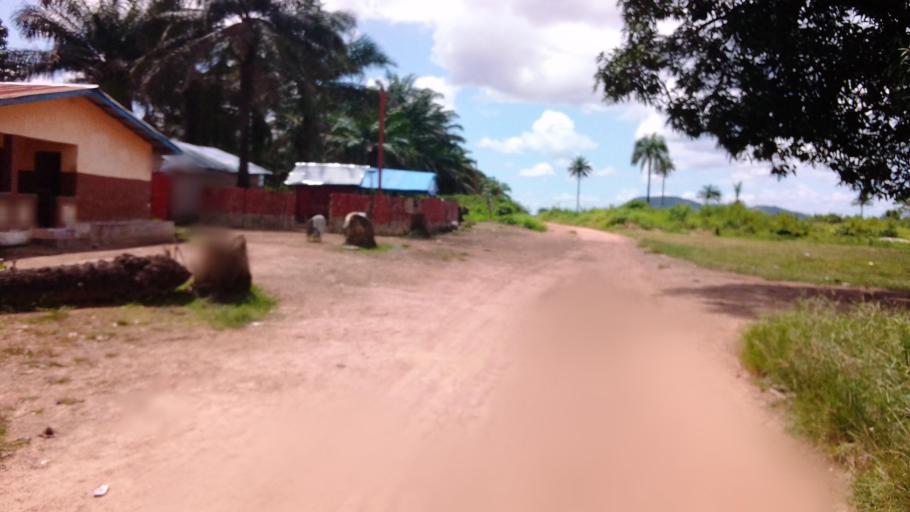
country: SL
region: Northern Province
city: Makeni
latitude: 8.8756
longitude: -12.0114
